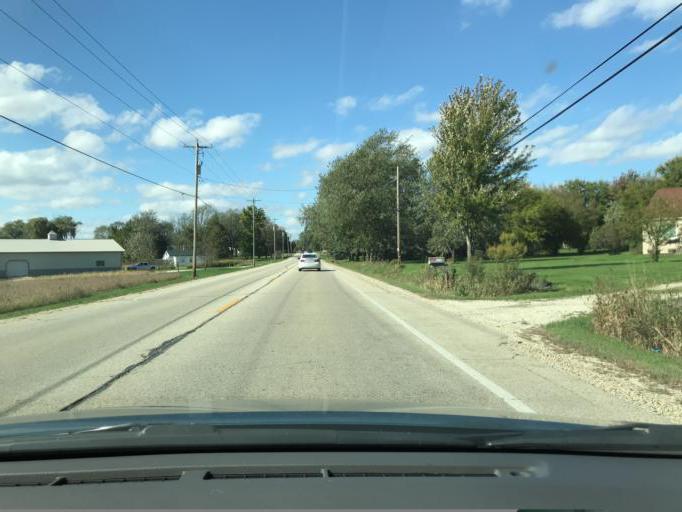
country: US
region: Wisconsin
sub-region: Kenosha County
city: Somers
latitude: 42.6079
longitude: -87.9332
